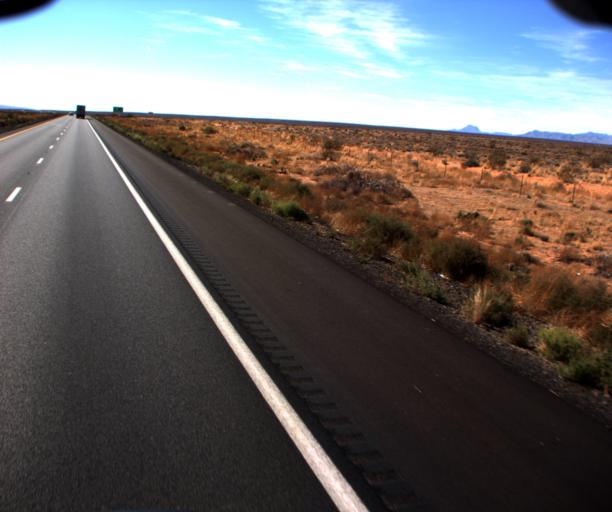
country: US
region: Arizona
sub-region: Mohave County
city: Beaver Dam
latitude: 36.8834
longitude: -113.9432
